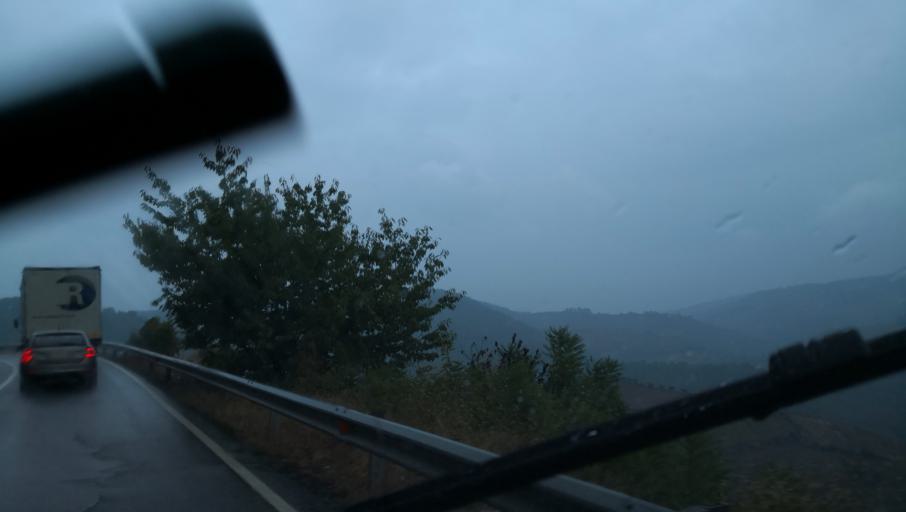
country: PT
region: Vila Real
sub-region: Vila Real
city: Vila Real
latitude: 41.2308
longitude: -7.7272
